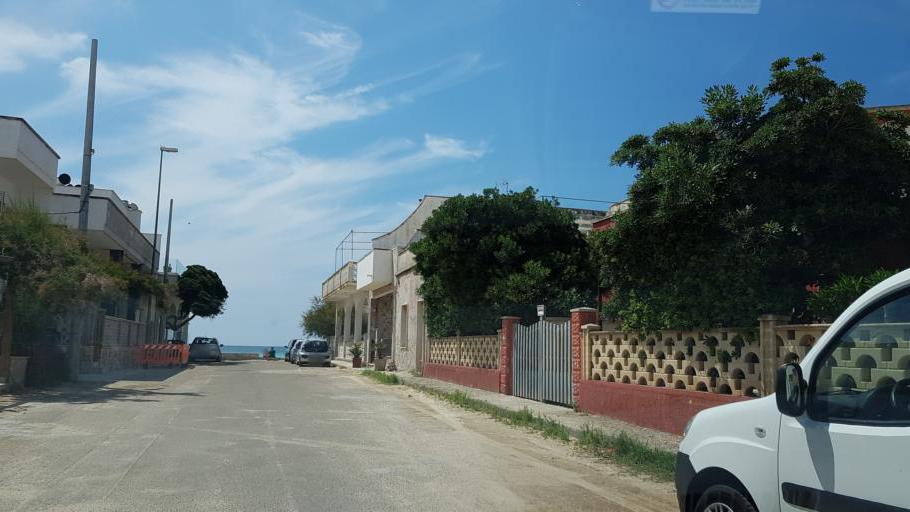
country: IT
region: Apulia
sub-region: Provincia di Lecce
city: Porto Cesareo
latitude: 40.2869
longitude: 17.8506
